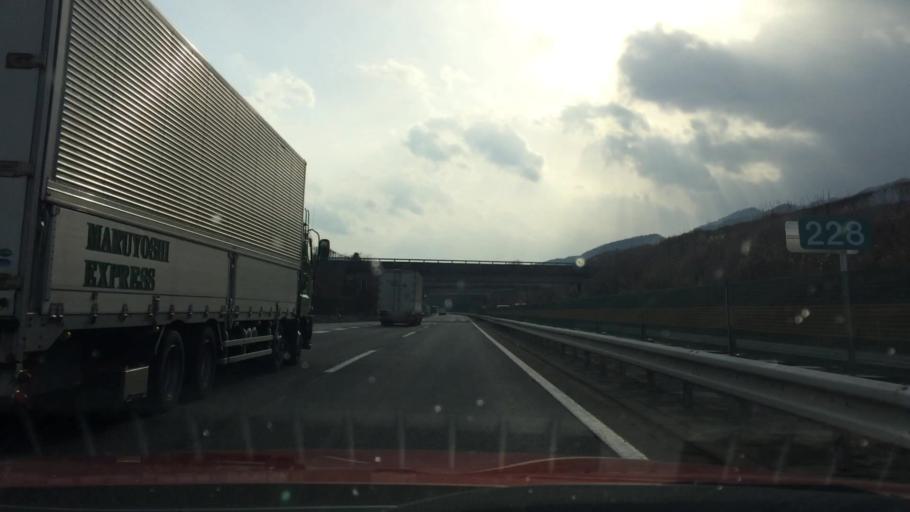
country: JP
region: Nagano
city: Ina
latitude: 35.6760
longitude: 137.9069
